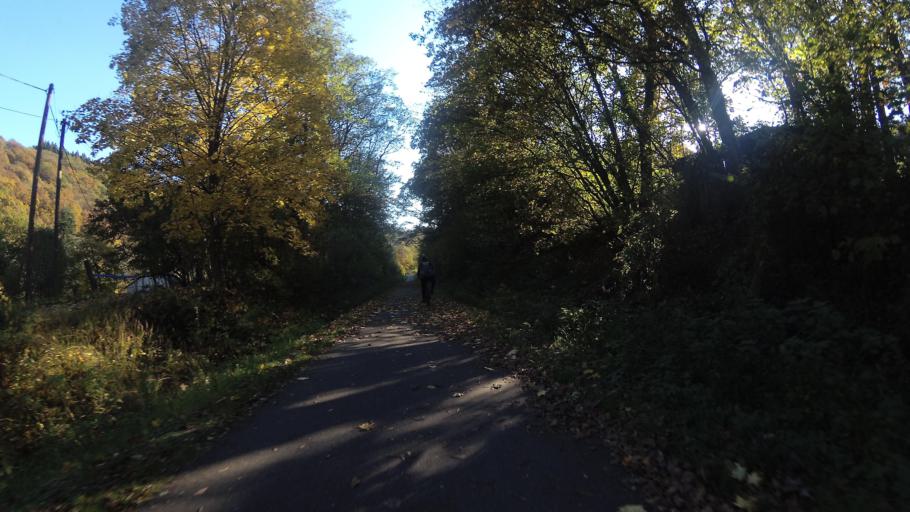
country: DE
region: Rheinland-Pfalz
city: Gutweiler
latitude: 49.7244
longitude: 6.7364
